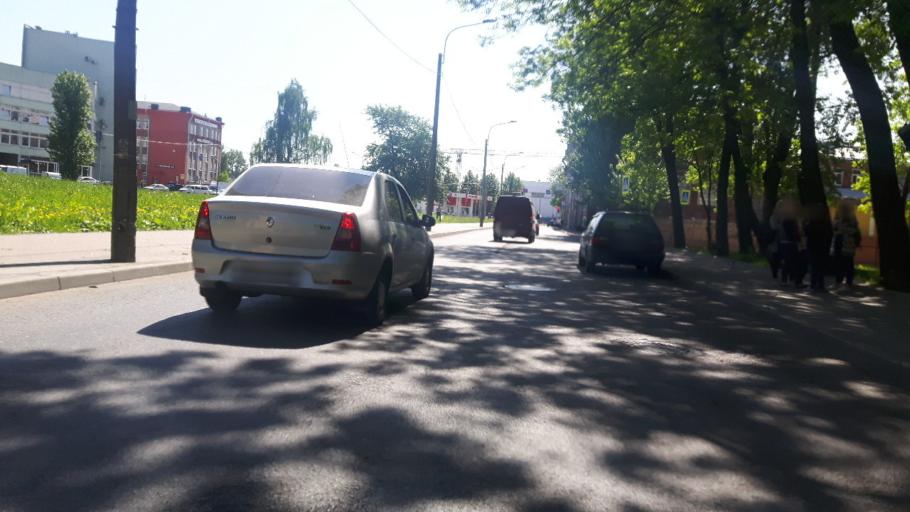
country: RU
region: St.-Petersburg
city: Admiralteisky
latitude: 59.8986
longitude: 30.2874
